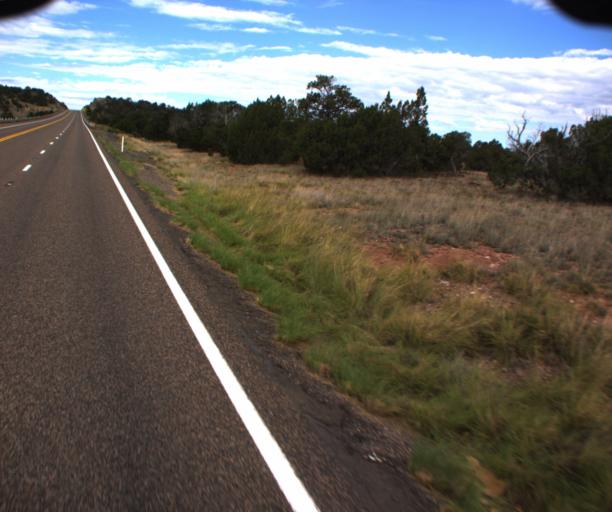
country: US
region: Arizona
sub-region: Apache County
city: Springerville
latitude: 34.1510
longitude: -109.1671
